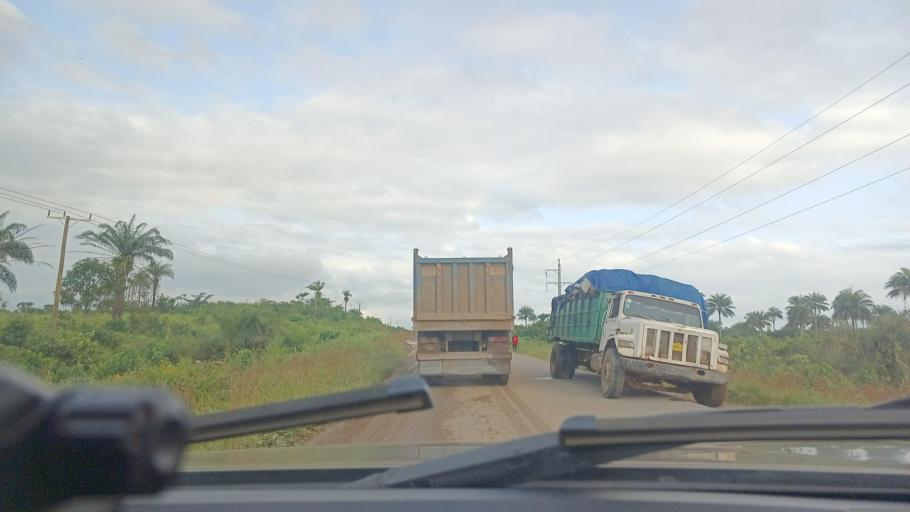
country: LR
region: Montserrado
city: Monrovia
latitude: 6.5742
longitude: -10.8826
